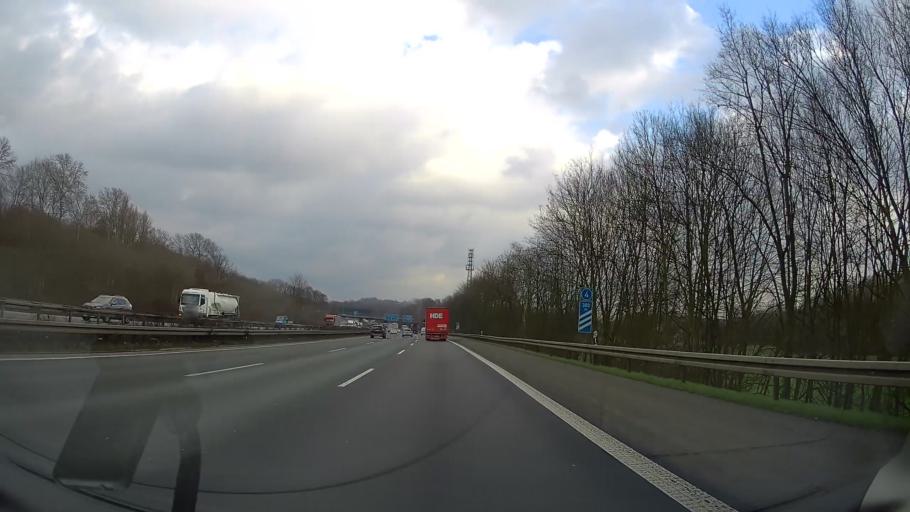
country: DE
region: North Rhine-Westphalia
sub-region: Regierungsbezirk Munster
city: Gladbeck
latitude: 51.5529
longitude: 6.9592
